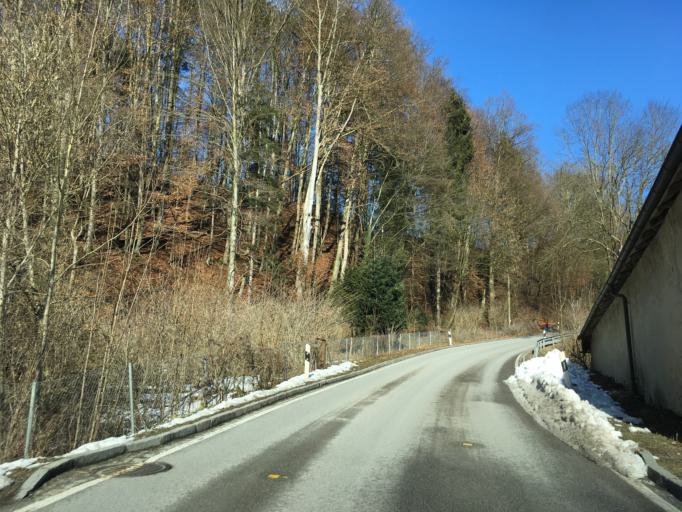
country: DE
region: Bavaria
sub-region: Upper Bavaria
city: Ramerberg
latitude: 48.0039
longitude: 12.1450
